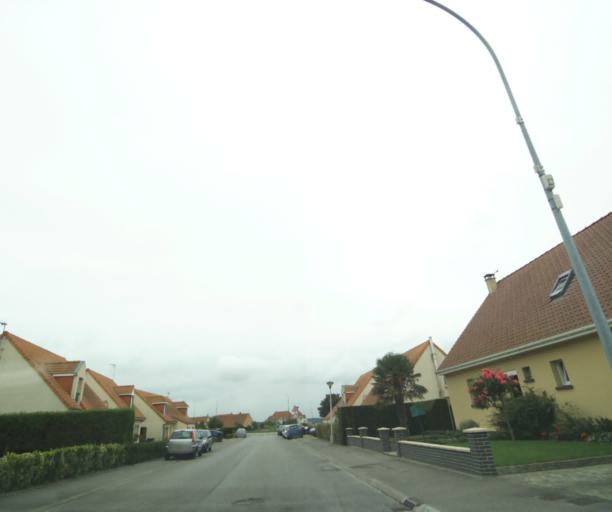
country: FR
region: Nord-Pas-de-Calais
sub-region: Departement du Pas-de-Calais
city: Etaples
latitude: 50.5162
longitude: 1.6534
